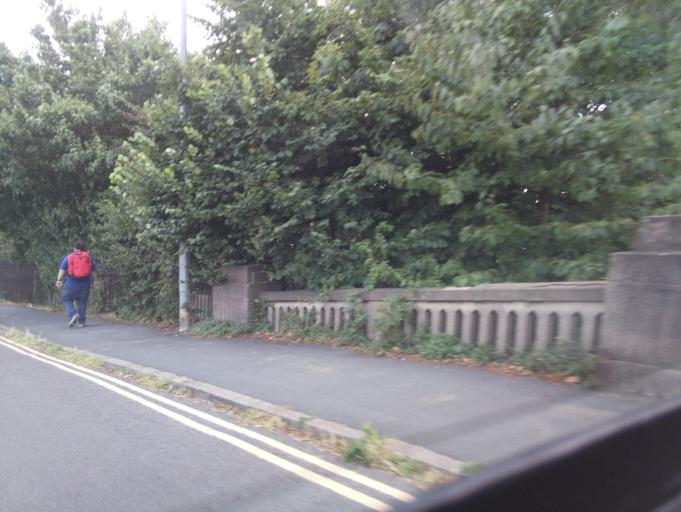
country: GB
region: England
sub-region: Leicestershire
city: Loughborough
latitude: 52.7782
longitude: -1.2020
